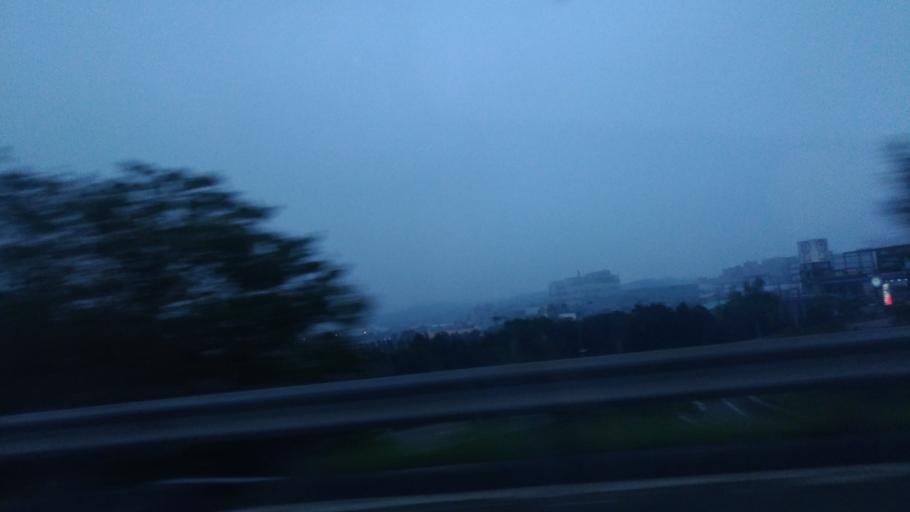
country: TW
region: Taiwan
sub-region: Hsinchu
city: Hsinchu
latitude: 24.7322
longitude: 120.9060
